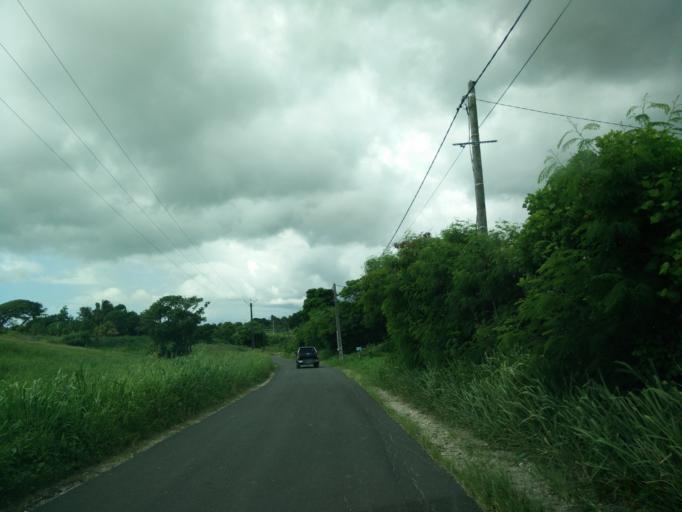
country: GP
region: Guadeloupe
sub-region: Guadeloupe
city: Le Moule
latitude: 16.3024
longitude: -61.3382
